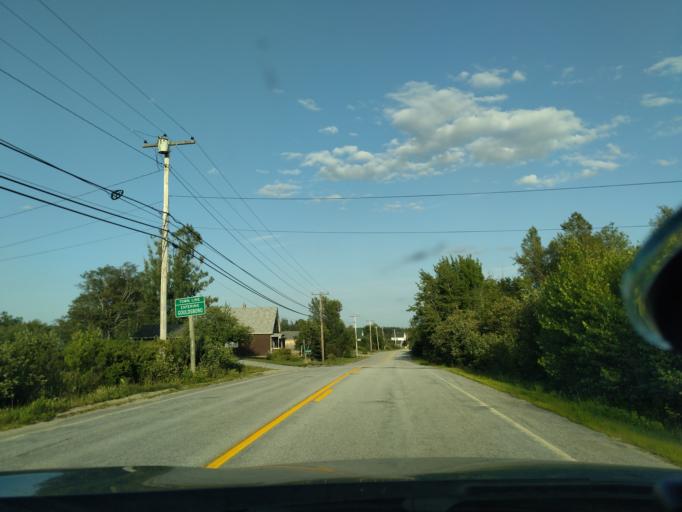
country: US
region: Maine
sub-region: Hancock County
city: Gouldsboro
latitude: 44.3908
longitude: -68.0457
